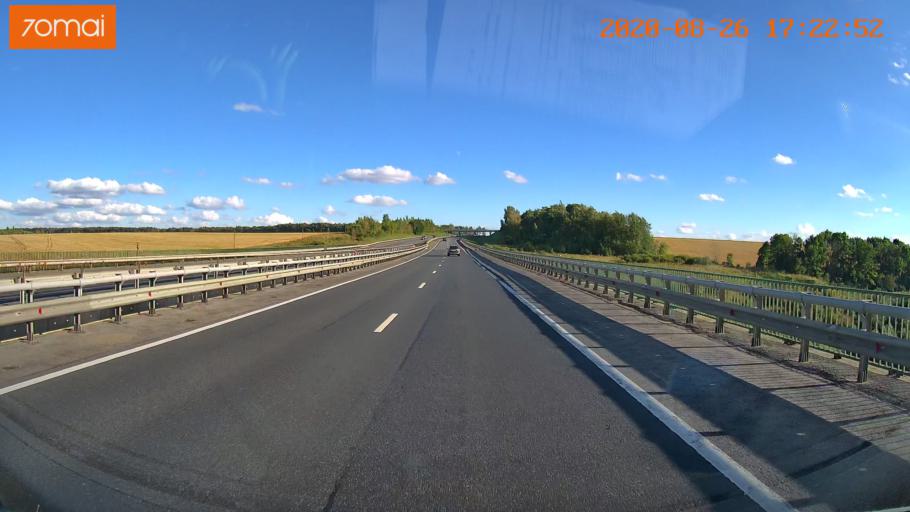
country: RU
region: Tula
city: Volovo
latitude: 53.5434
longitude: 38.1136
